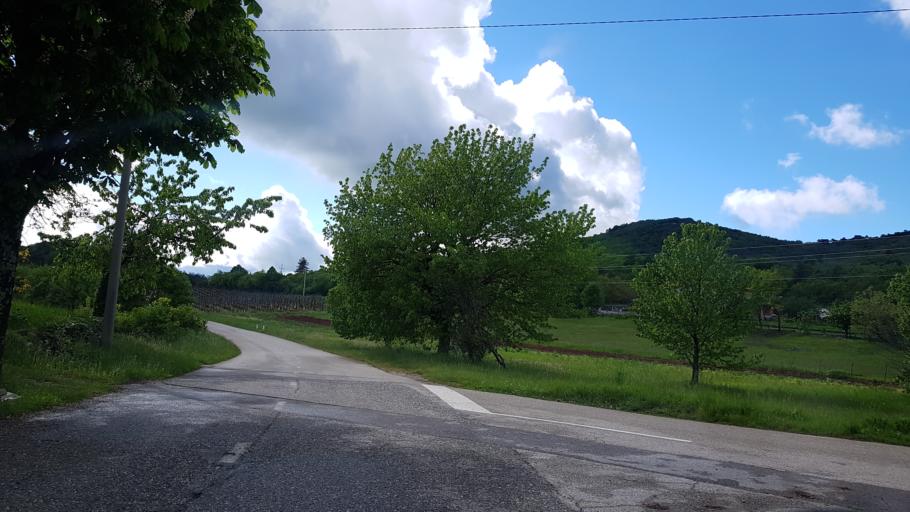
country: SI
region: Nova Gorica
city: Prvacina
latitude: 45.8476
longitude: 13.7010
